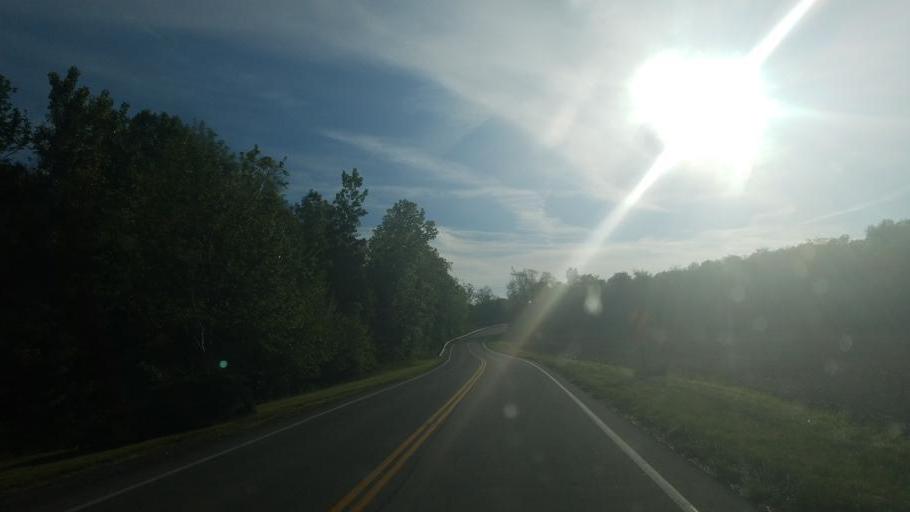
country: US
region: Ohio
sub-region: Ross County
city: Frankfort
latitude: 39.4276
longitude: -83.2358
